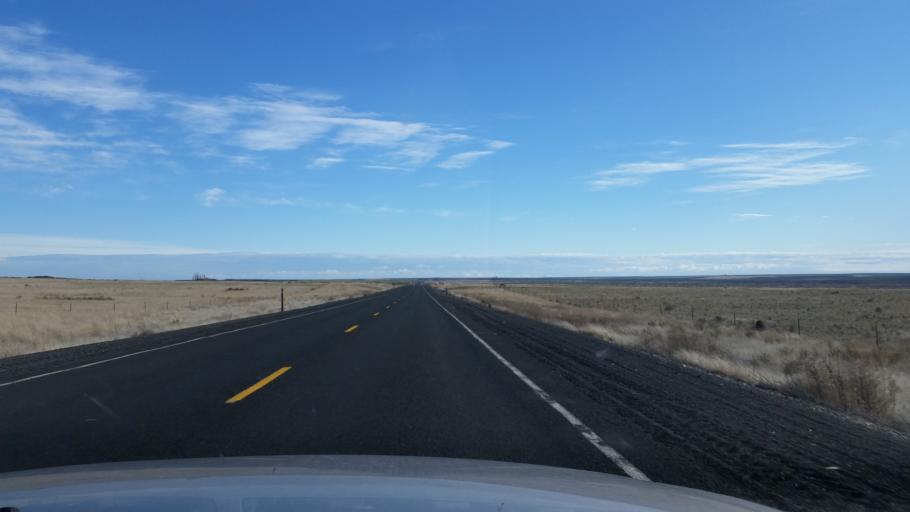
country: US
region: Washington
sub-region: Grant County
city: Warden
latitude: 47.3473
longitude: -118.9268
